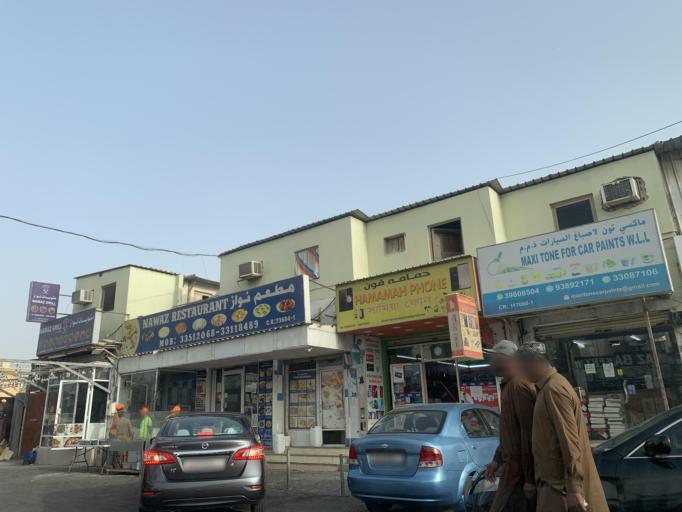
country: BH
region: Northern
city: Madinat `Isa
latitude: 26.1830
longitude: 50.5291
